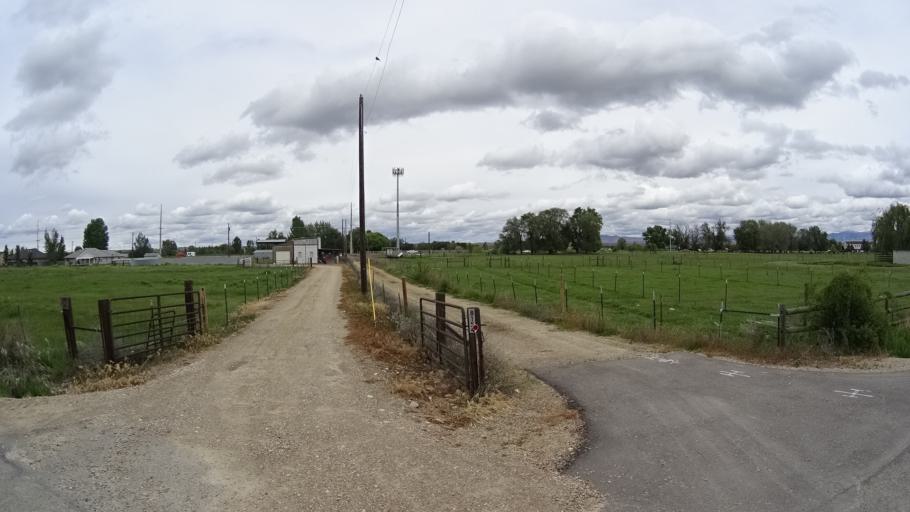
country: US
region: Idaho
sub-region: Ada County
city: Star
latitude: 43.6896
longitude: -116.4556
